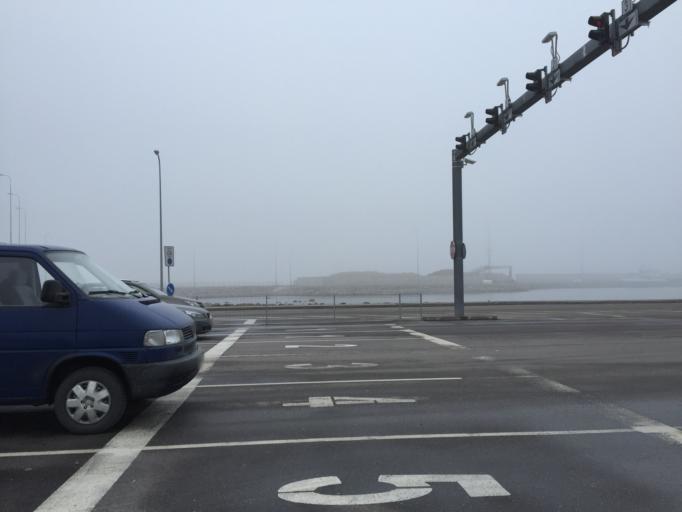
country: EE
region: Laeaene
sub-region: Lihula vald
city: Lihula
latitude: 58.5744
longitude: 23.5098
